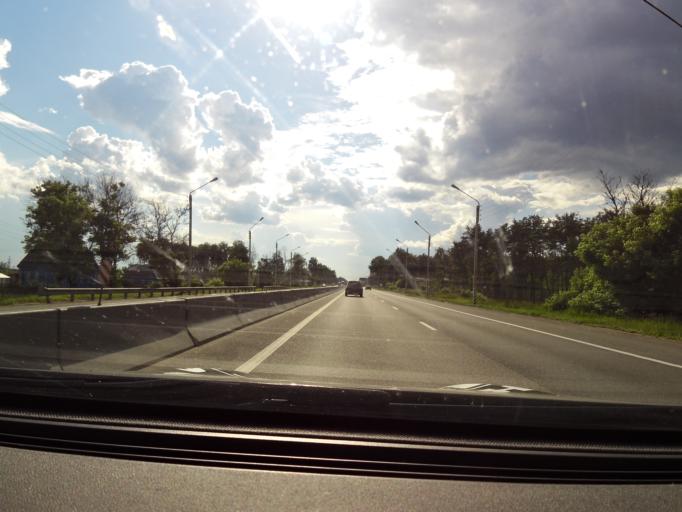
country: RU
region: Nizjnij Novgorod
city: Babino
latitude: 56.3023
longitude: 43.5721
